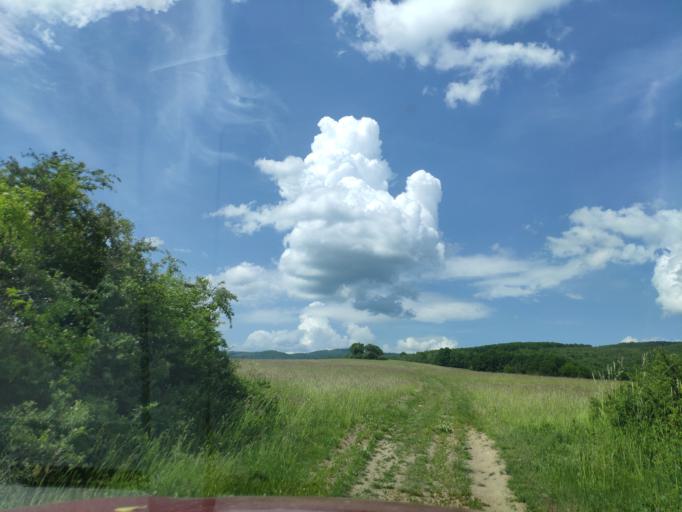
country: SK
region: Kosicky
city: Medzev
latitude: 48.7157
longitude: 20.9631
